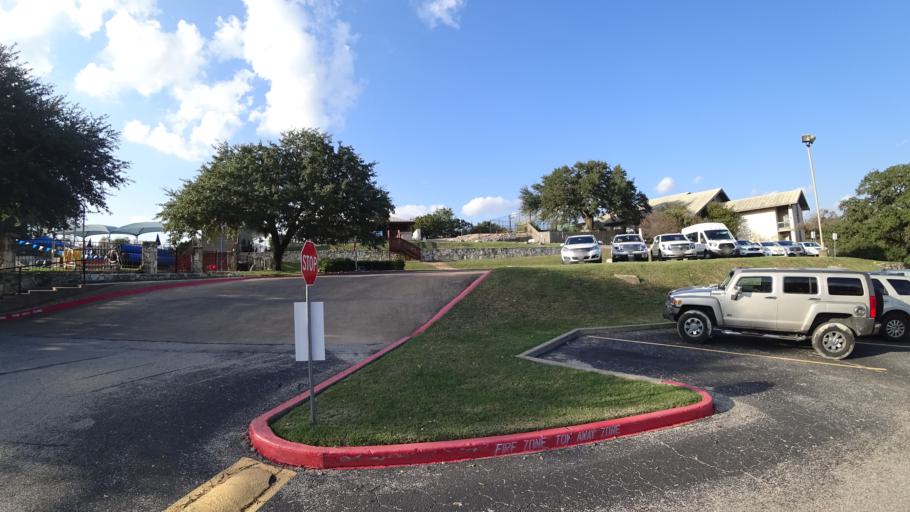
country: US
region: Texas
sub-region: Travis County
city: Lost Creek
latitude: 30.2747
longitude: -97.8495
